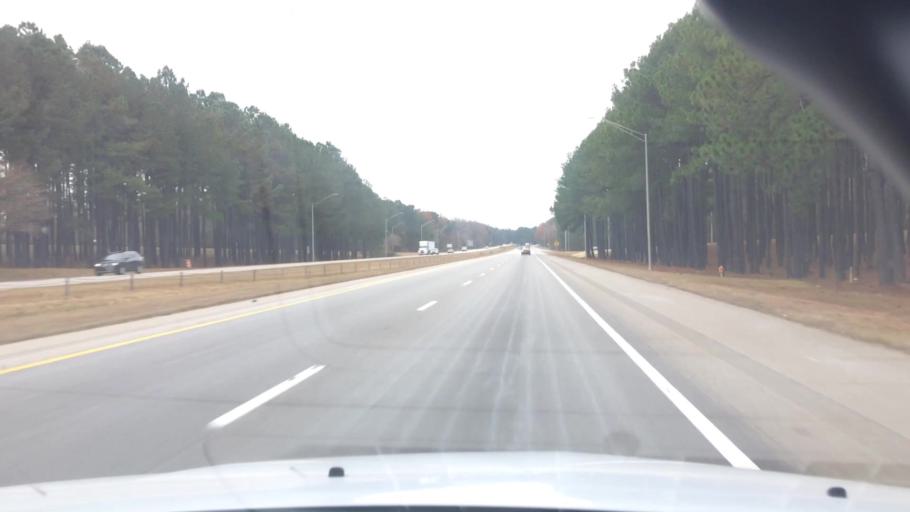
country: US
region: North Carolina
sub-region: Wilson County
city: Wilson
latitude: 35.7636
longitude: -78.0040
